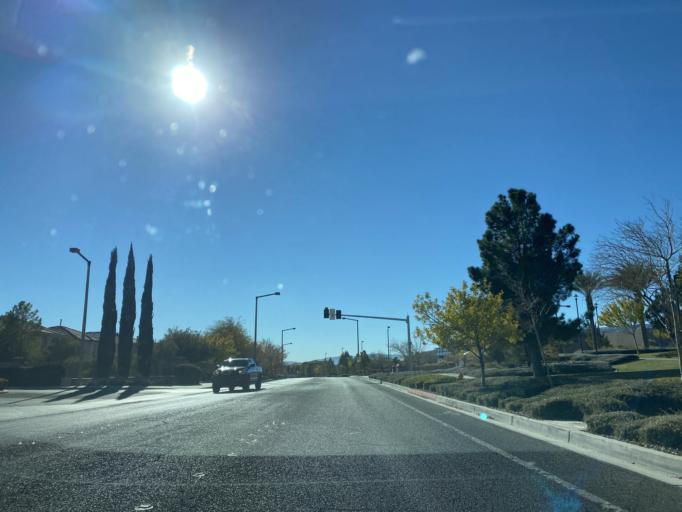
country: US
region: Nevada
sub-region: Clark County
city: Summerlin South
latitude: 36.1693
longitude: -115.3430
